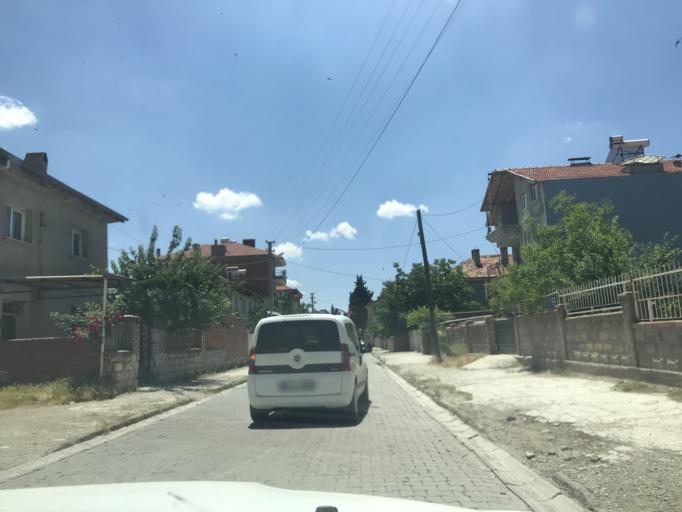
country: TR
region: Denizli
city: Civril
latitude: 38.3024
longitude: 29.7442
